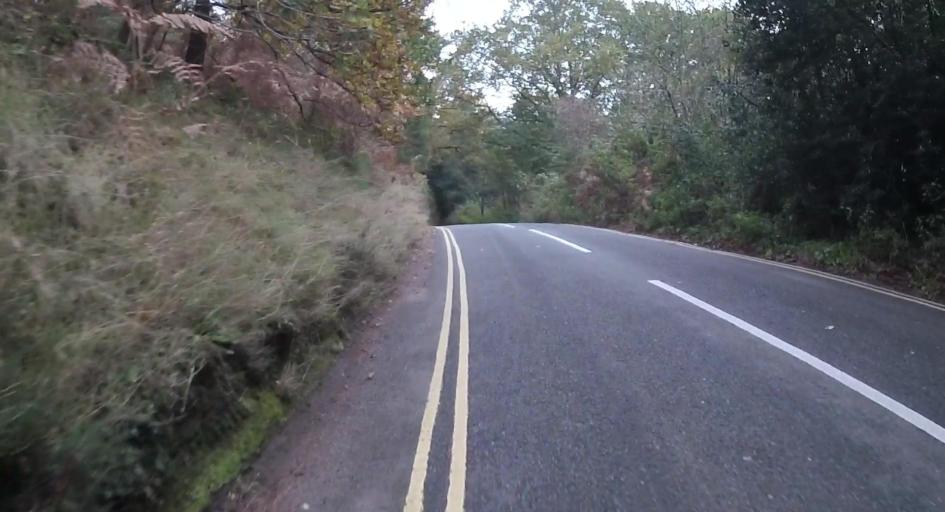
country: GB
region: England
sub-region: Surrey
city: Churt
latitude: 51.1622
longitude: -0.7946
